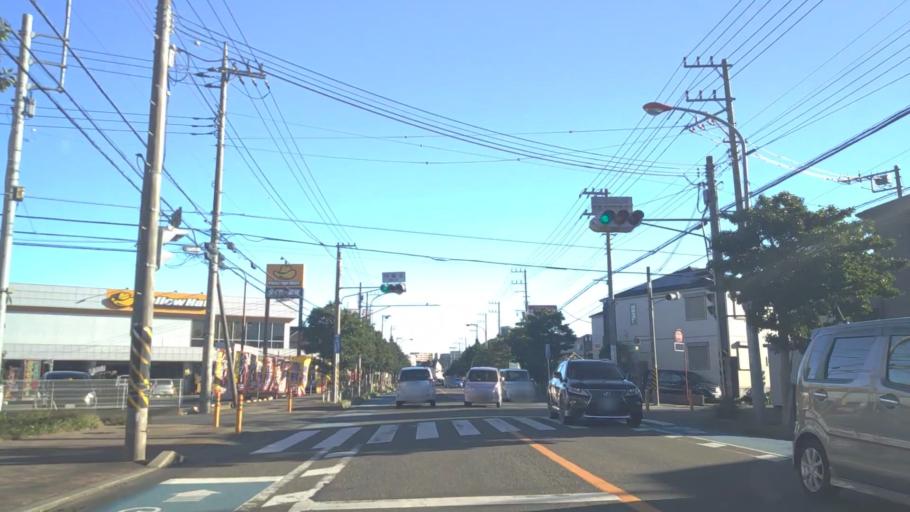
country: JP
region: Kanagawa
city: Chigasaki
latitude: 35.3457
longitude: 139.3978
